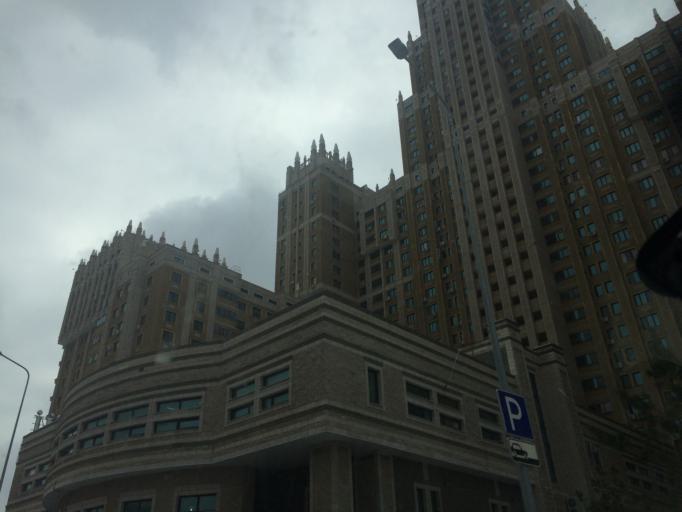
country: KZ
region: Astana Qalasy
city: Astana
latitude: 51.1412
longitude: 71.4153
